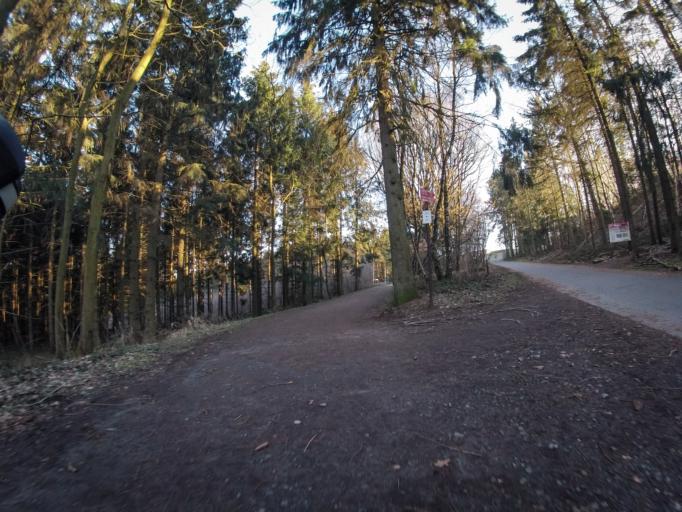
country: DE
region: Lower Saxony
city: Wallenhorst
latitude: 52.3221
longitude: 8.0261
